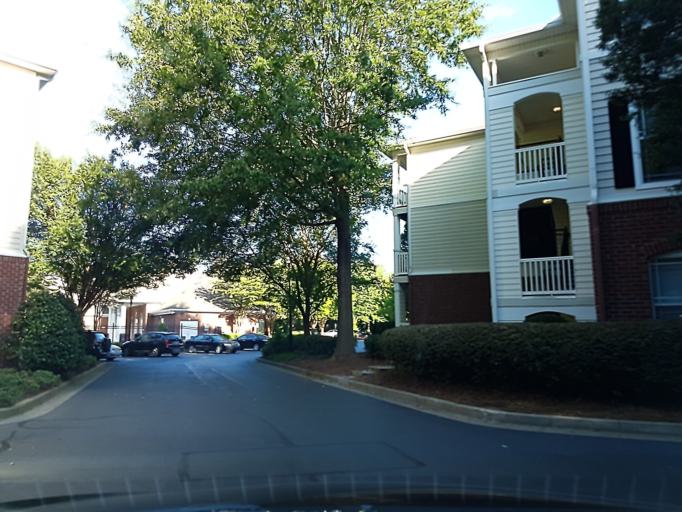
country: US
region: Georgia
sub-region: DeKalb County
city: Chamblee
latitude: 33.8608
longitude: -84.2865
